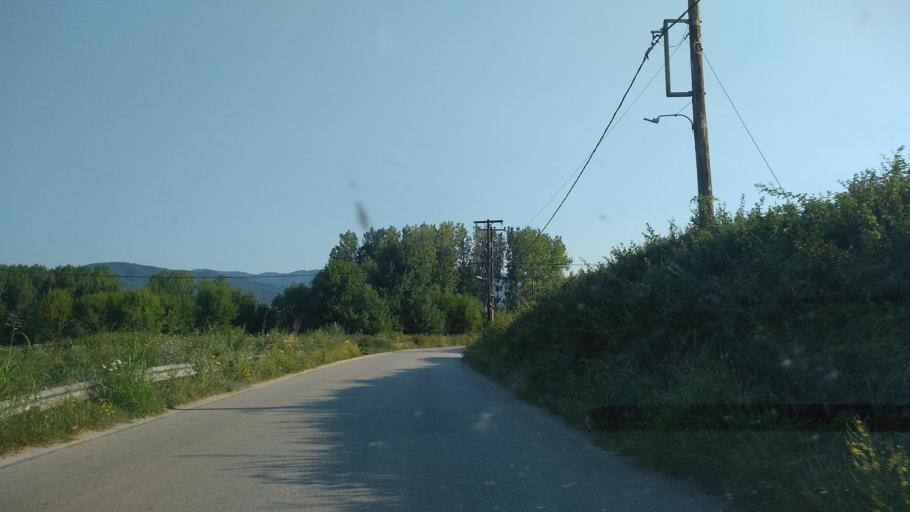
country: GR
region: Central Macedonia
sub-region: Nomos Thessalonikis
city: Stavros
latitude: 40.6798
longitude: 23.6867
